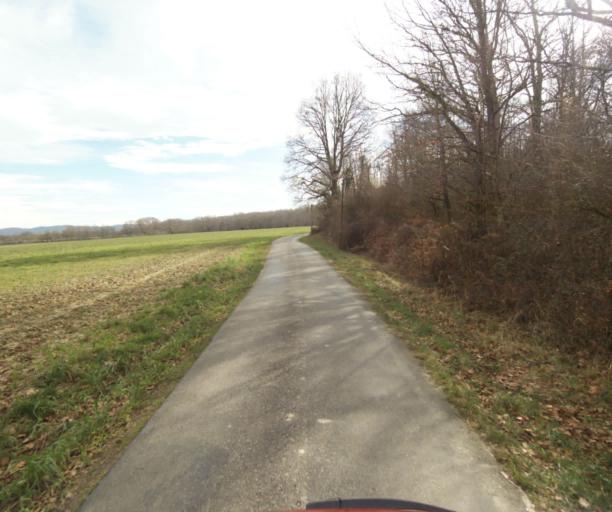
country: FR
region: Midi-Pyrenees
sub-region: Departement de l'Ariege
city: La Tour-du-Crieu
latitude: 43.0909
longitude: 1.7430
